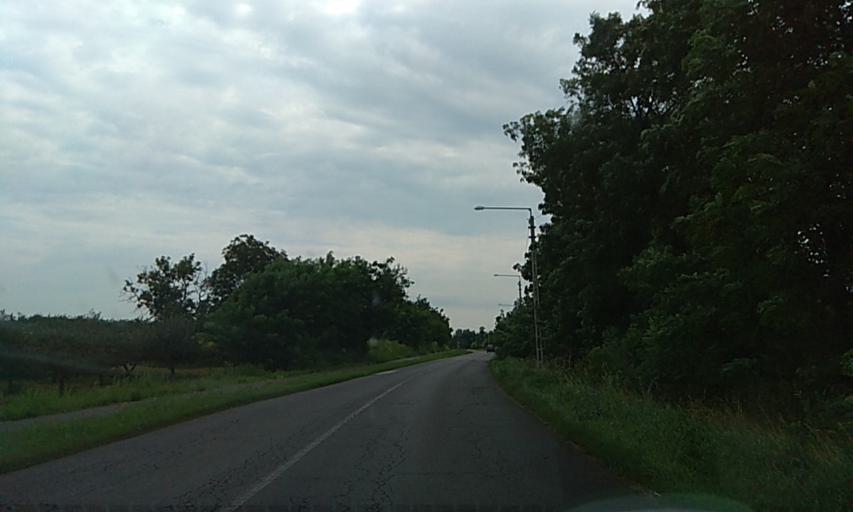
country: HU
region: Szabolcs-Szatmar-Bereg
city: Kotaj
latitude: 48.0095
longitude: 21.6939
